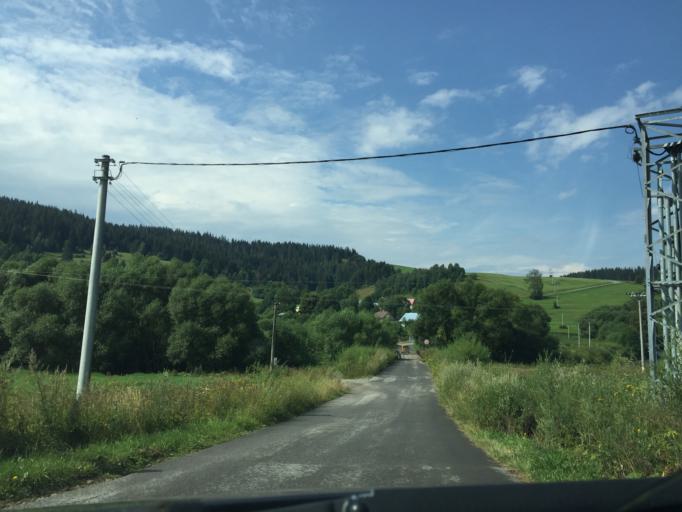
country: PL
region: Silesian Voivodeship
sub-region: Powiat zywiecki
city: Korbielow
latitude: 49.4345
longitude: 19.3169
